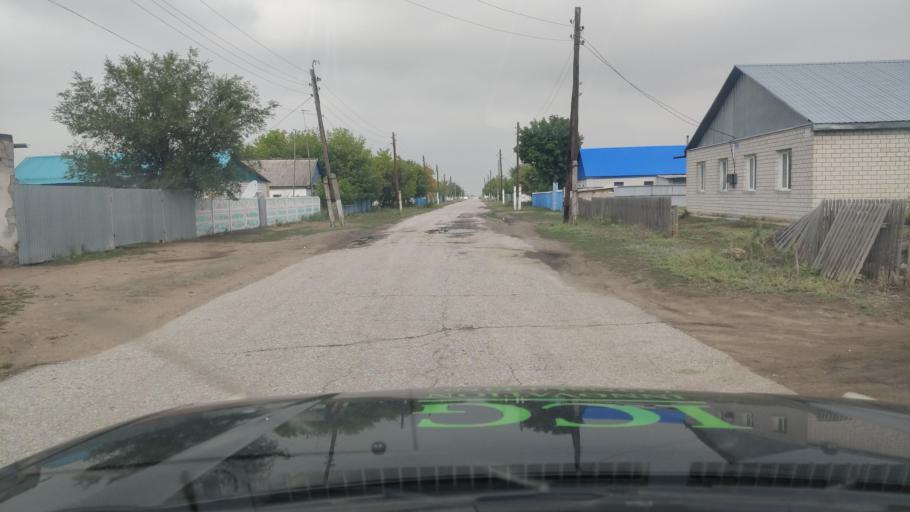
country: KZ
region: Pavlodar
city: Aksu
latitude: 51.9345
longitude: 77.2974
